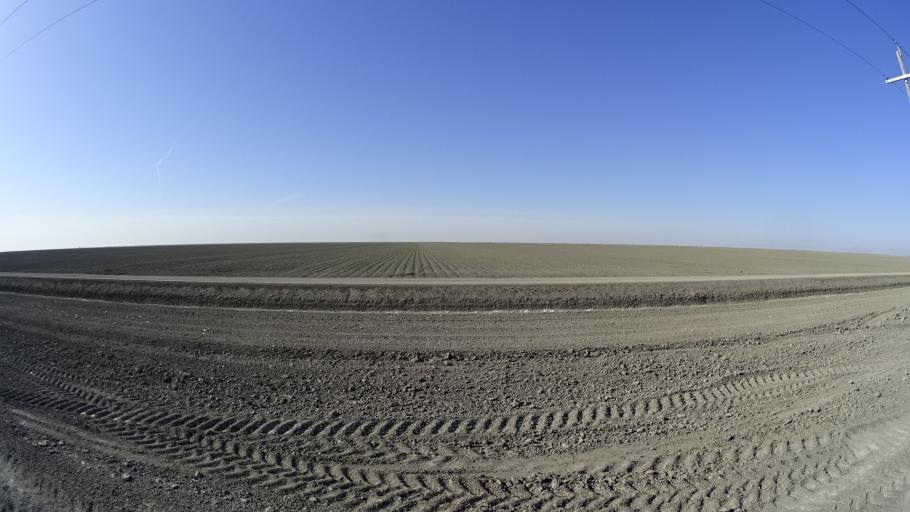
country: US
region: California
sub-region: Kings County
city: Corcoran
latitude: 36.0797
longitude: -119.6943
